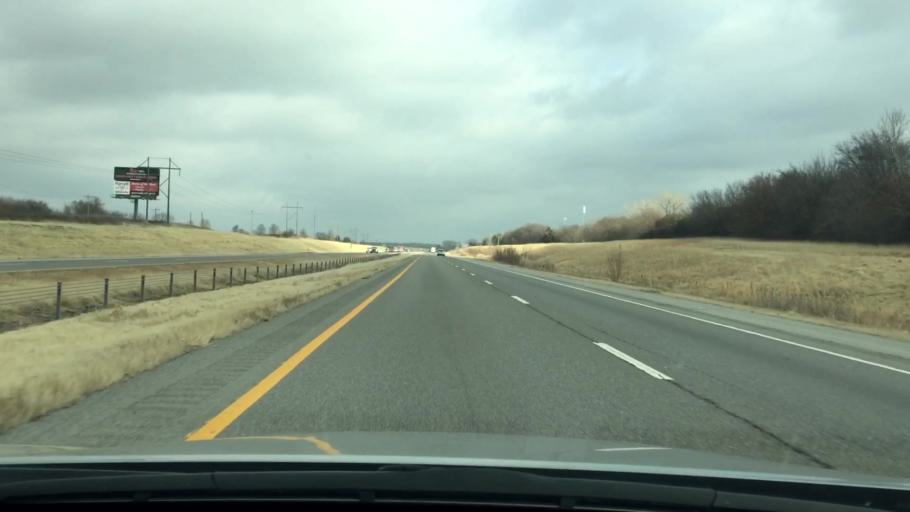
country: US
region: Oklahoma
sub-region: McClain County
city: Purcell
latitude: 35.0189
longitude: -97.3758
